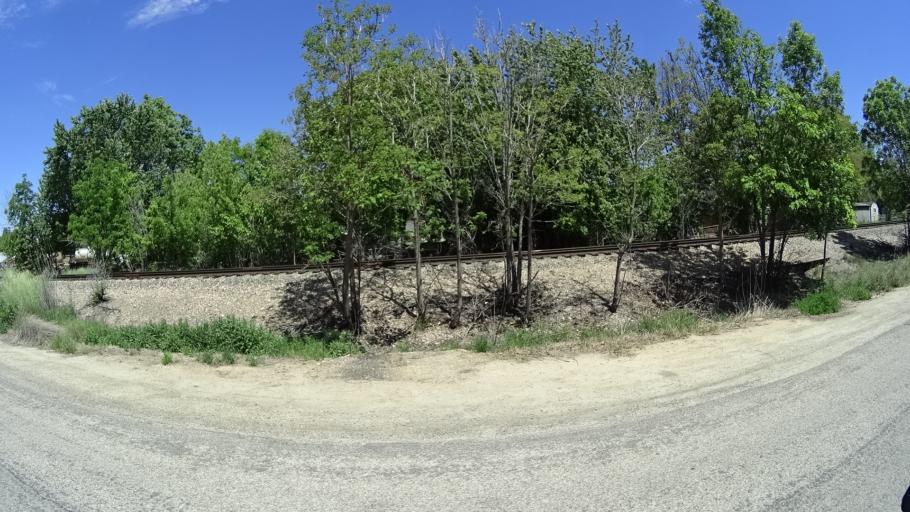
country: US
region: Idaho
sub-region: Ada County
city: Garden City
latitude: 43.6043
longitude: -116.2357
